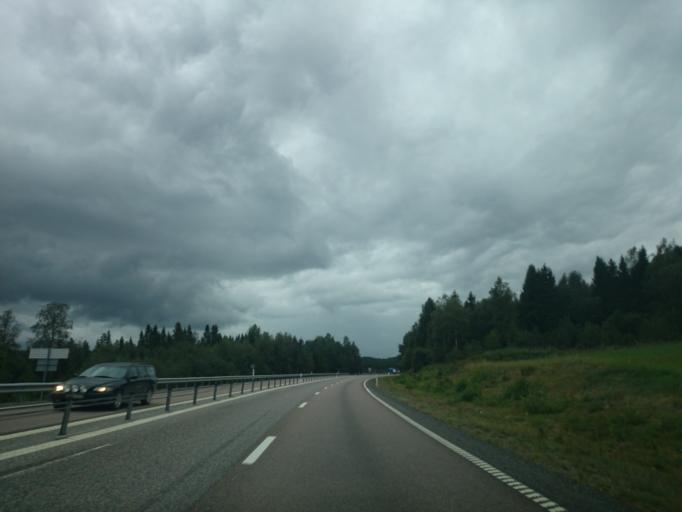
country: SE
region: Vaesternorrland
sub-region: Kramfors Kommun
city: Nordingra
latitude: 62.9671
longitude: 18.1572
